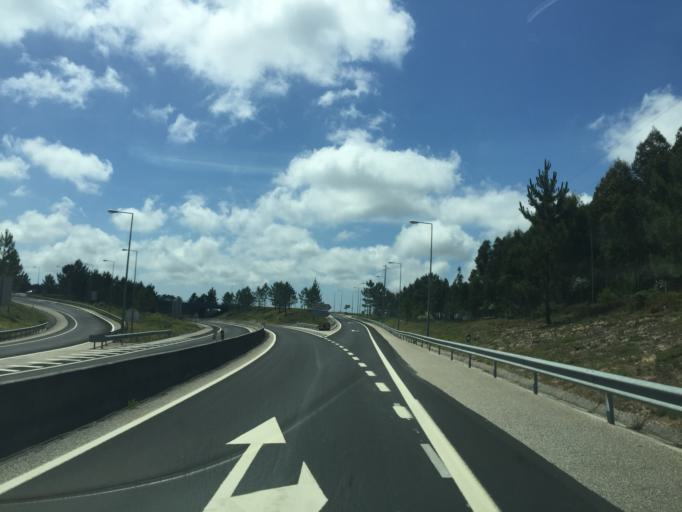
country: PT
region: Leiria
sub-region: Marinha Grande
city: Marinha Grande
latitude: 39.7152
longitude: -8.9211
